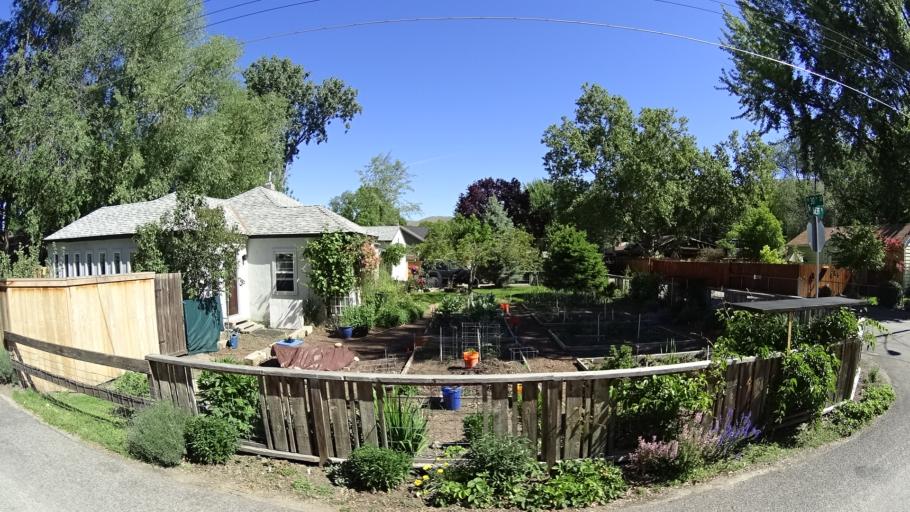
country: US
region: Idaho
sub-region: Ada County
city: Garden City
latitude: 43.6469
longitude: -116.2259
